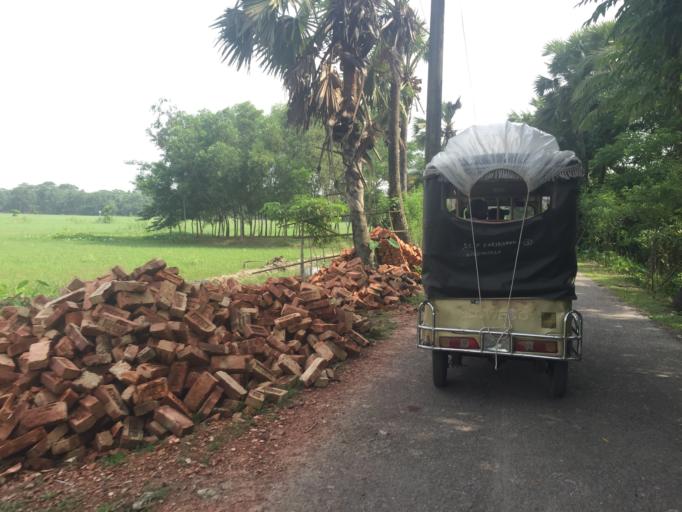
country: BD
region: Barisal
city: Mathba
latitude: 22.2465
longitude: 89.9132
